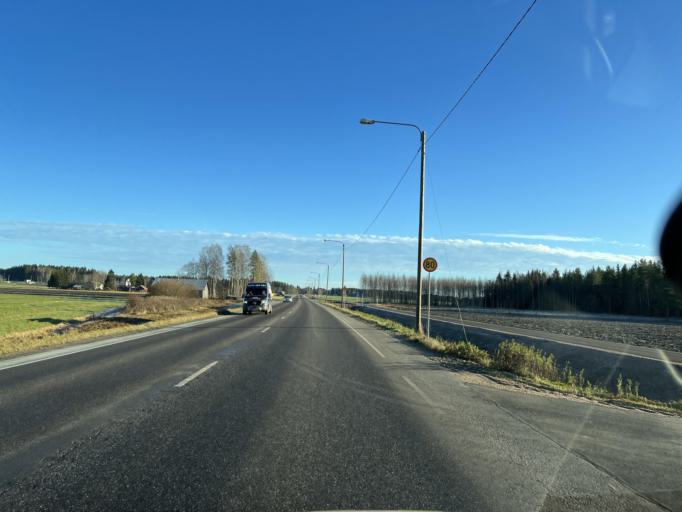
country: FI
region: Northern Ostrobothnia
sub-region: Nivala-Haapajaervi
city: Nivala
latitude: 63.9510
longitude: 24.8855
